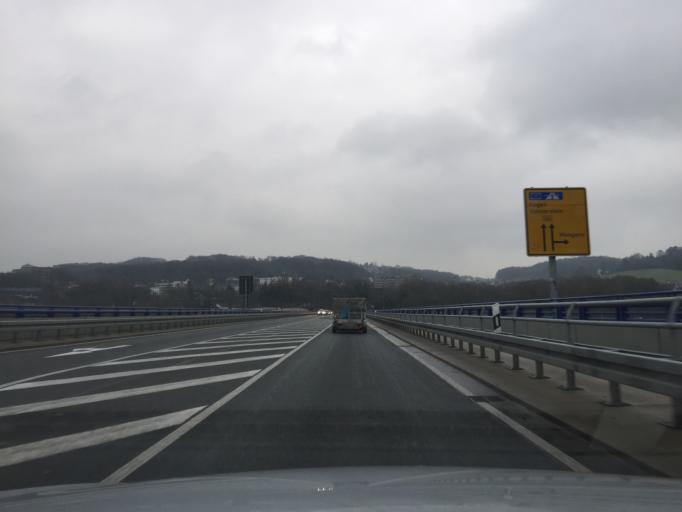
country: DE
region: North Rhine-Westphalia
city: Wetter (Ruhr)
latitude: 51.3898
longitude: 7.3788
